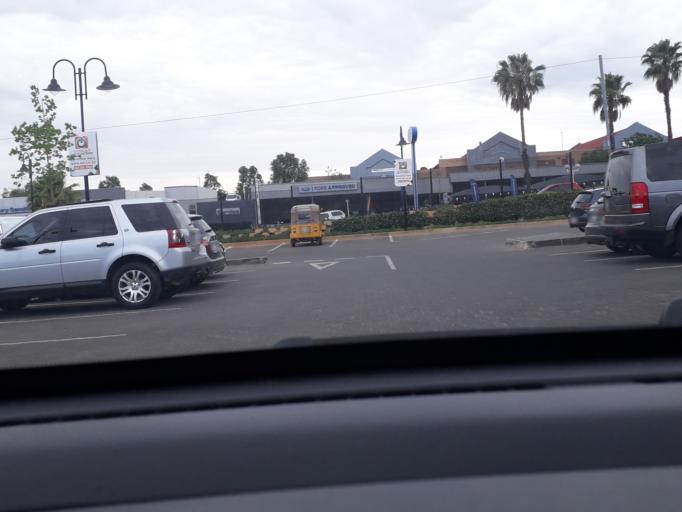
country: ZA
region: Gauteng
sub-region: City of Johannesburg Metropolitan Municipality
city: Midrand
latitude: -26.0357
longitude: 28.0510
